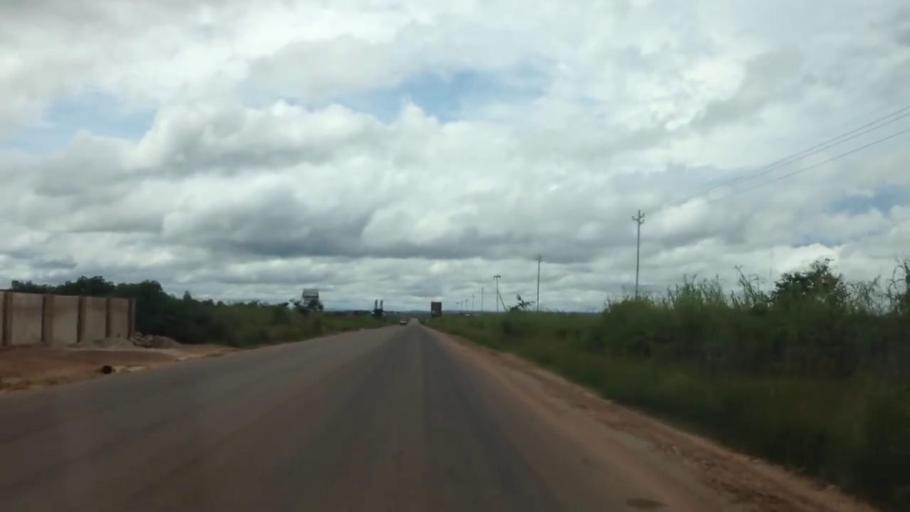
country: CD
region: Katanga
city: Kolwezi
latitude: -10.7475
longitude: 25.5147
